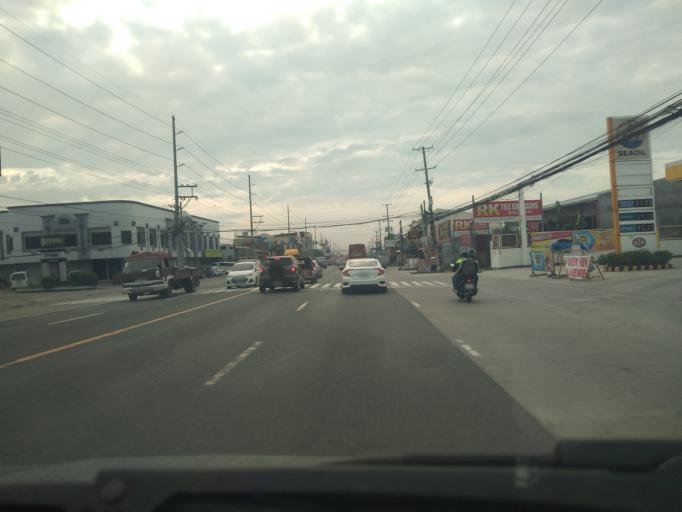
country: PH
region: Central Luzon
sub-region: Province of Pampanga
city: Bulaon
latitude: 15.0682
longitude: 120.6490
